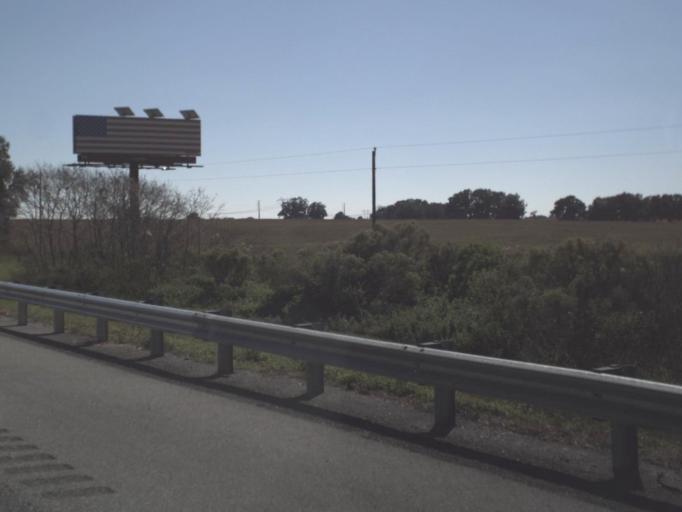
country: US
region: Florida
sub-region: Lake County
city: Leesburg
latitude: 28.7765
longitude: -81.9642
